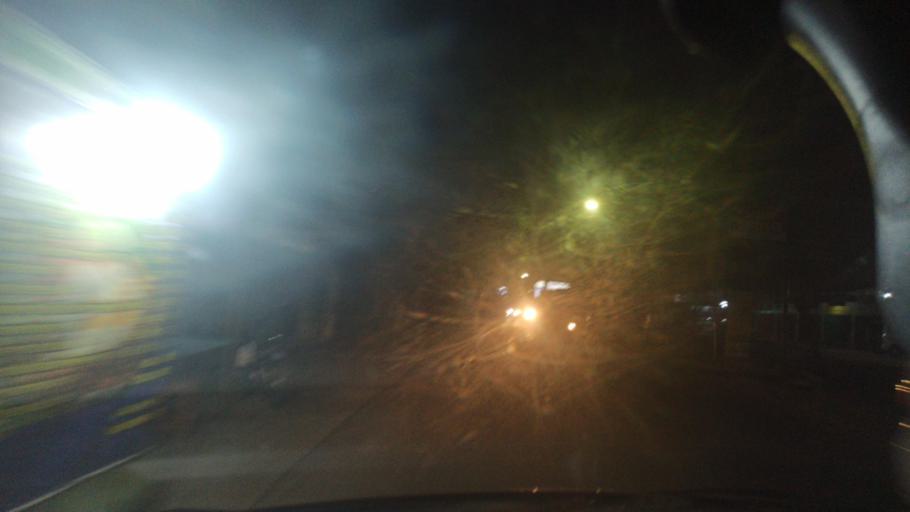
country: ID
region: South Sumatra
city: Palembang
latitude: -2.9263
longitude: 104.7860
